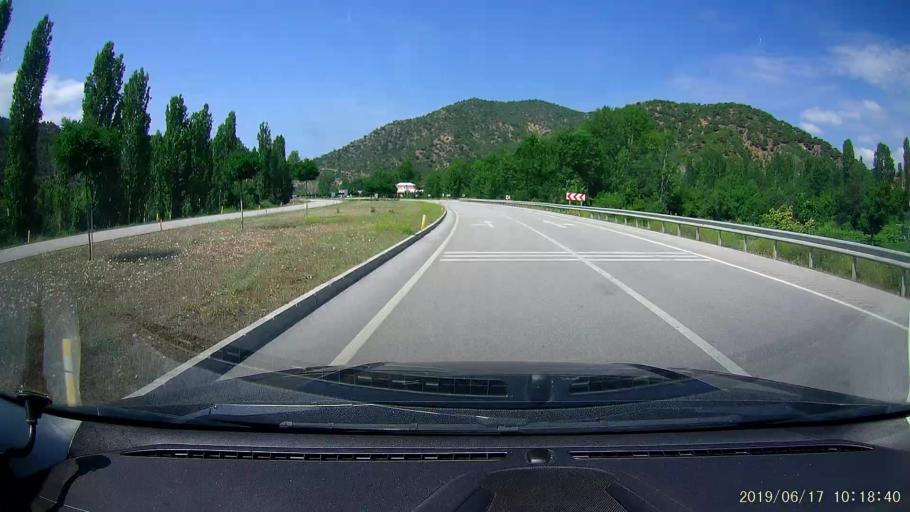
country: TR
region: Corum
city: Osmancik
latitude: 40.9770
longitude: 34.9160
